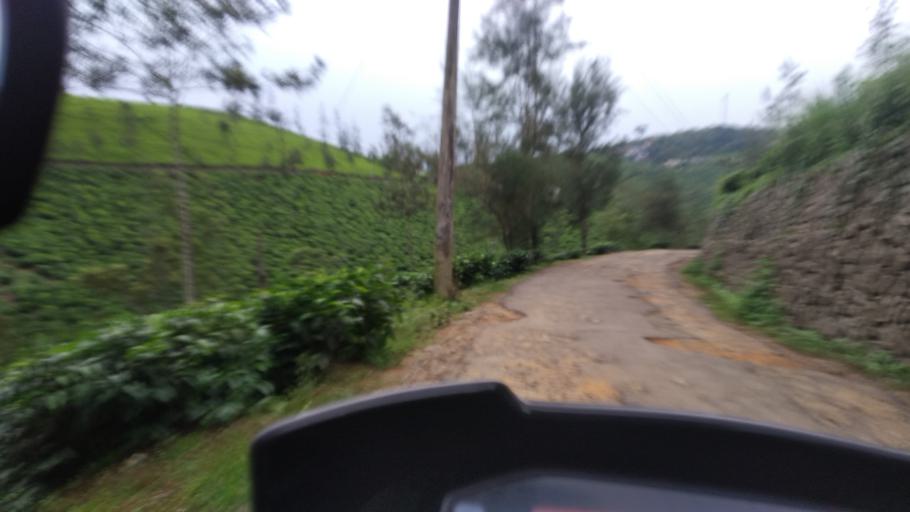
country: IN
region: Tamil Nadu
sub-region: Theni
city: Gudalur
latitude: 9.5416
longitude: 77.0401
